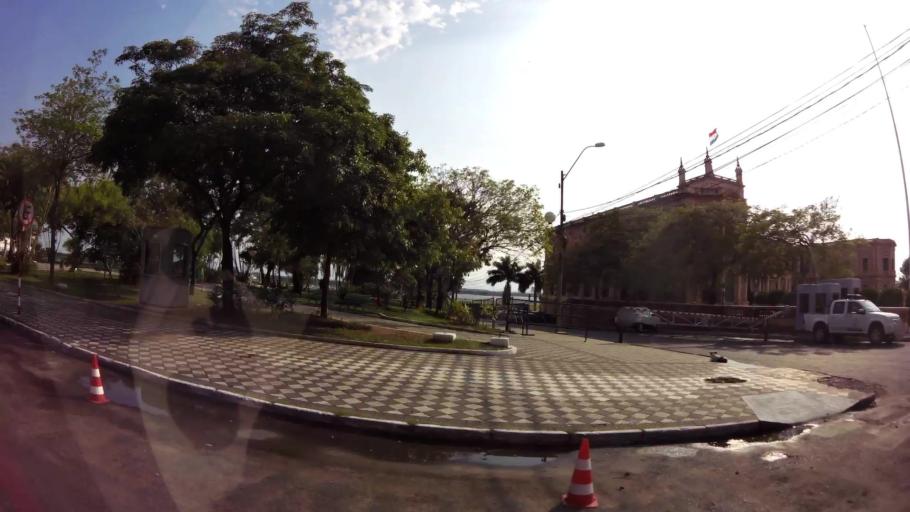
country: PY
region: Asuncion
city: Asuncion
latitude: -25.2775
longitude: -57.6381
